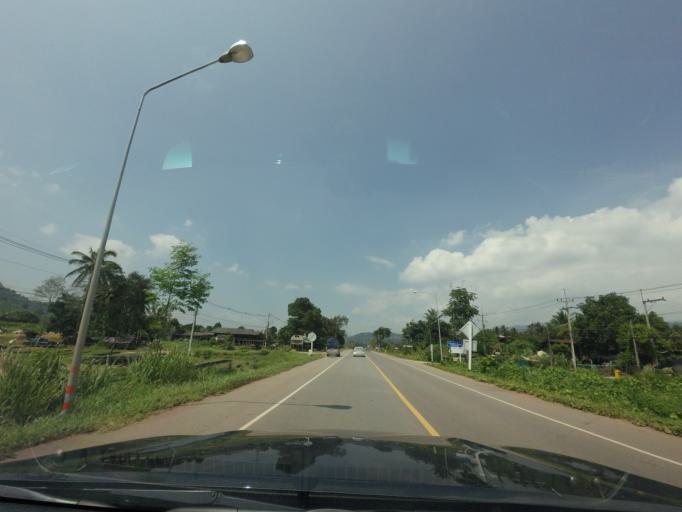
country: TH
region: Loei
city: Phu Ruea
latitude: 17.4565
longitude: 101.3925
